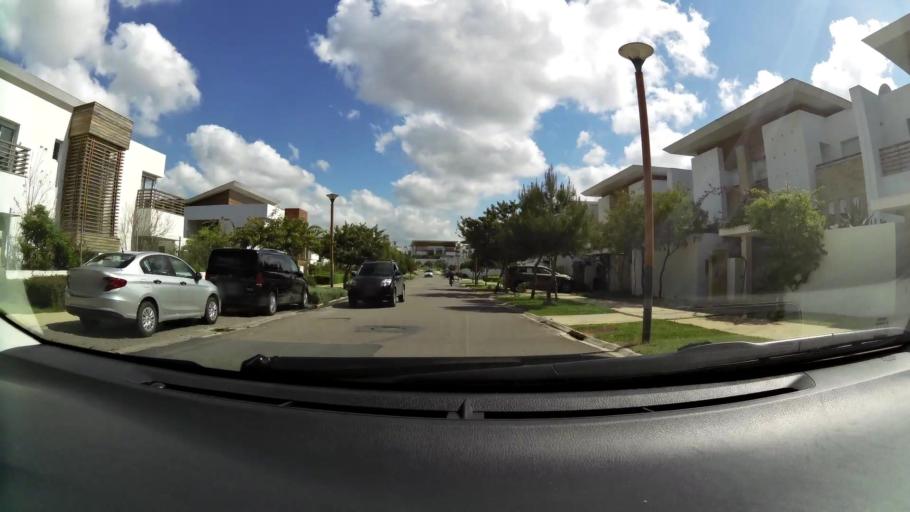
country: MA
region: Grand Casablanca
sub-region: Nouaceur
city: Bouskoura
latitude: 33.4890
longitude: -7.5997
